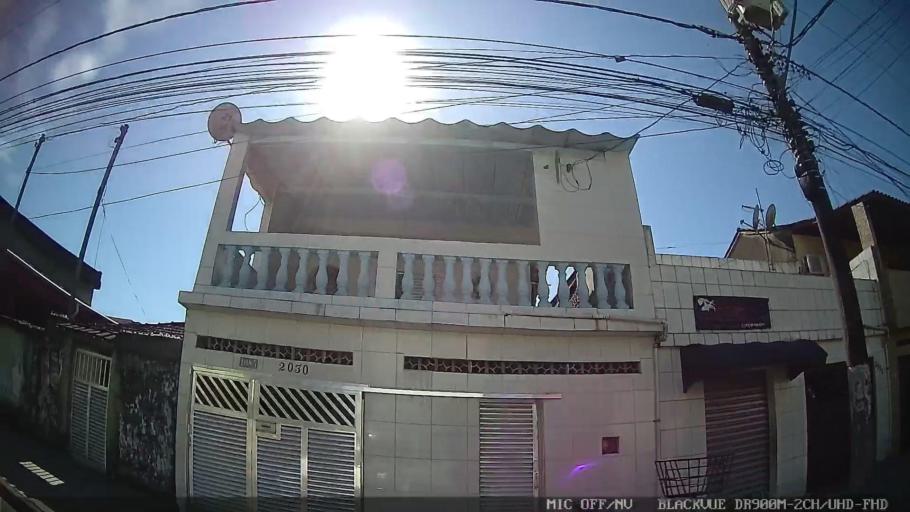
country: BR
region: Sao Paulo
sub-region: Guaruja
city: Guaruja
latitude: -23.9500
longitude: -46.2830
